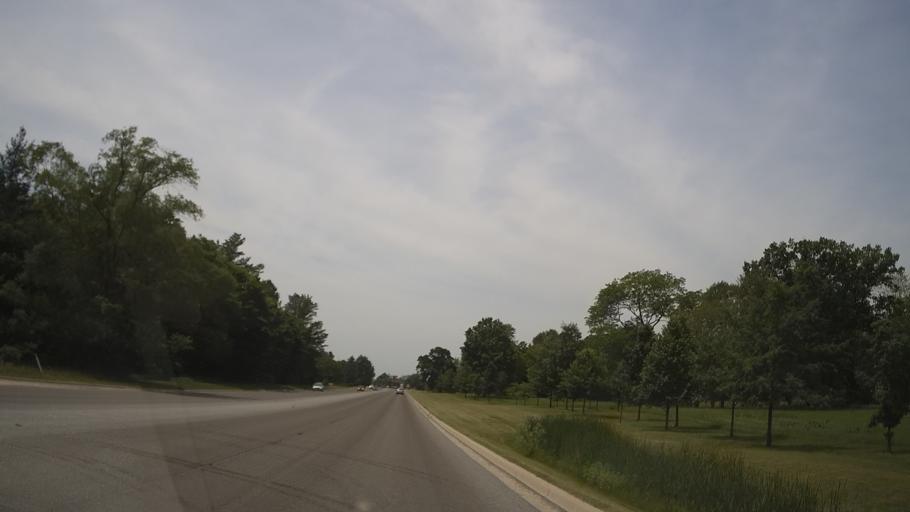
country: US
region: Michigan
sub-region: Washtenaw County
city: Milan
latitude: 42.1569
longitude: -83.6891
